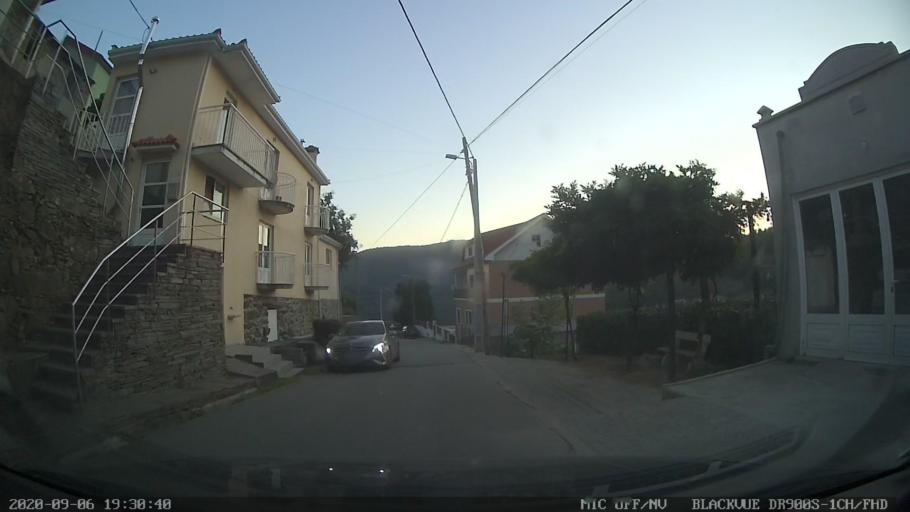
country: PT
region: Vila Real
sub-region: Mesao Frio
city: Mesao Frio
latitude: 41.1842
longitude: -7.9006
